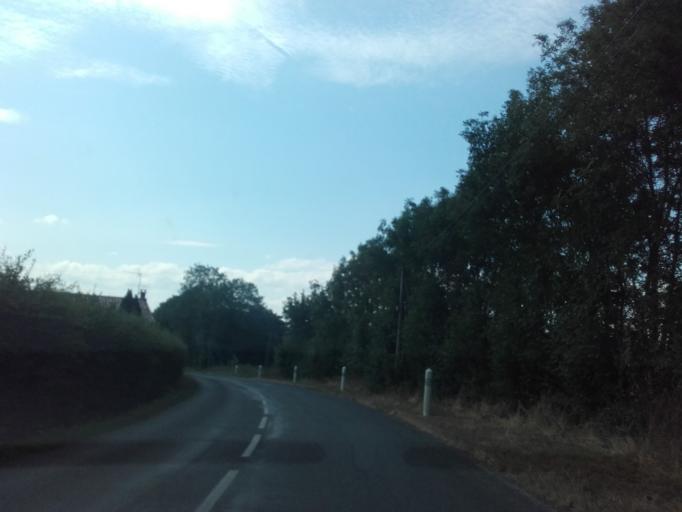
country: FR
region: Rhone-Alpes
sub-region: Departement de l'Ain
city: Chatillon-sur-Chalaronne
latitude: 46.0940
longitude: 5.0112
